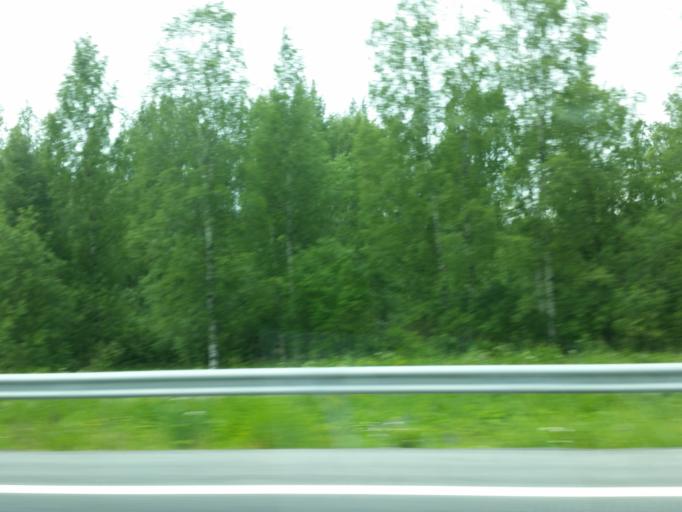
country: FI
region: Northern Savo
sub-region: Kuopio
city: Kuopio
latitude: 62.9628
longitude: 27.6951
